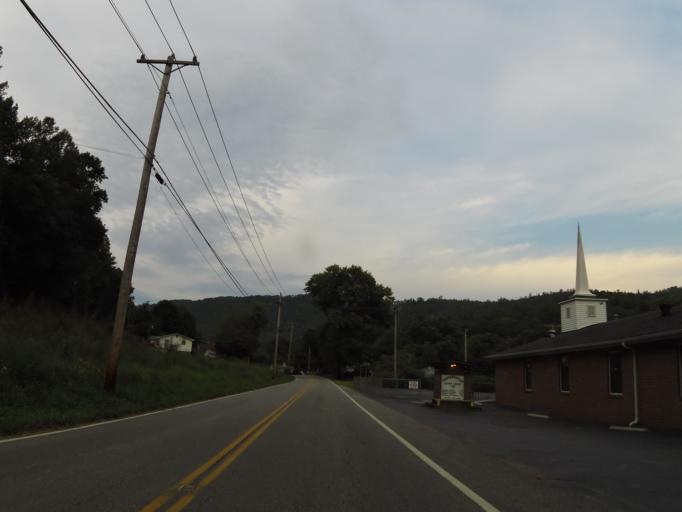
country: US
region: Tennessee
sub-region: Anderson County
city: Rocky Top
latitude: 36.1952
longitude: -84.1740
